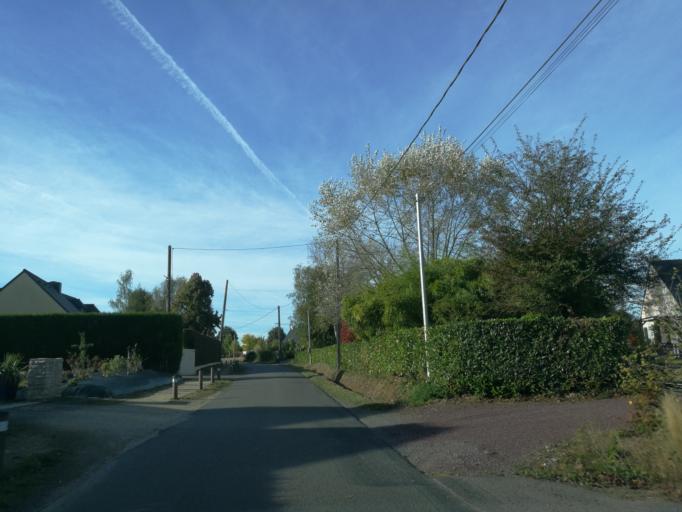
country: FR
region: Brittany
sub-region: Departement d'Ille-et-Vilaine
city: Bedee
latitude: 48.1934
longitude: -1.9498
